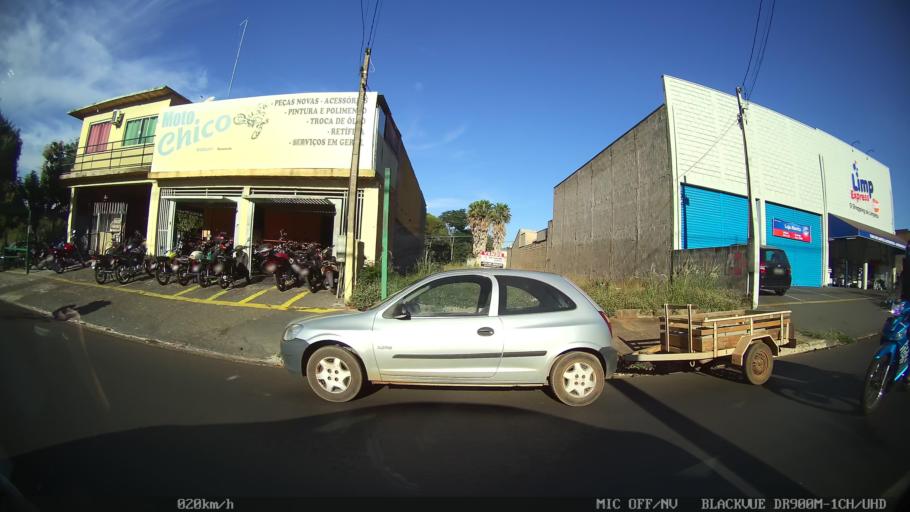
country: BR
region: Sao Paulo
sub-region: Araraquara
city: Araraquara
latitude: -21.7474
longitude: -48.1614
